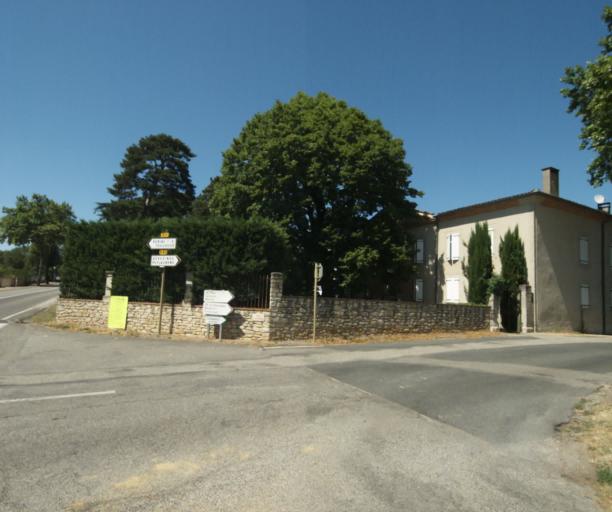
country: FR
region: Midi-Pyrenees
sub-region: Departement de la Haute-Garonne
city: Saint-Felix-Lauragais
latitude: 43.4772
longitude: 1.9268
